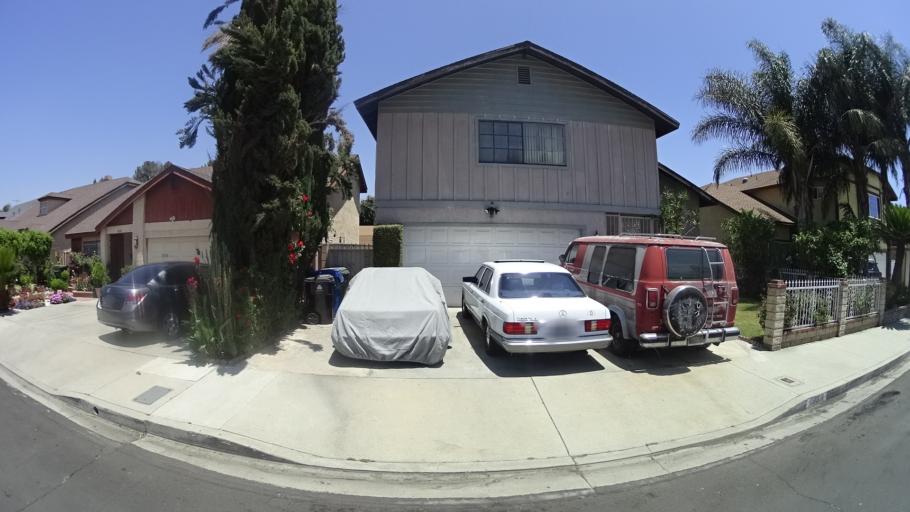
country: US
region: California
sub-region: Los Angeles County
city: Van Nuys
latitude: 34.2265
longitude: -118.4602
